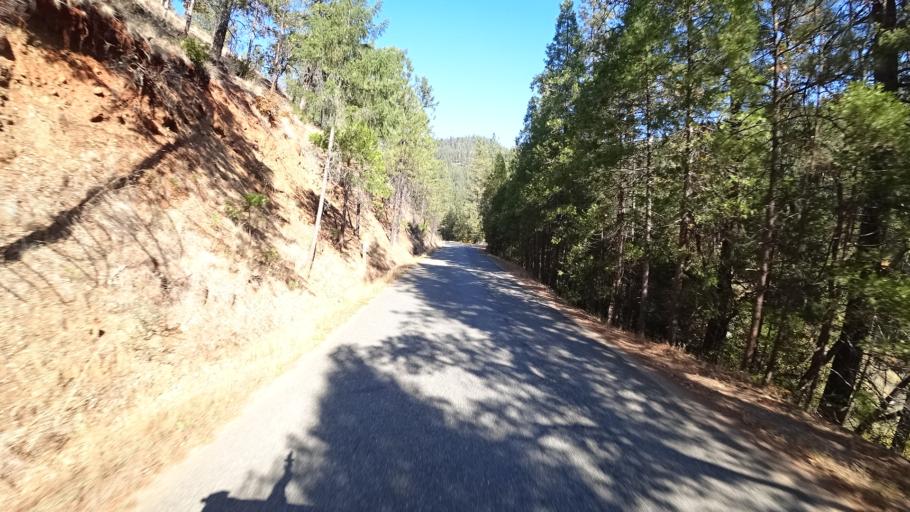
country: US
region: California
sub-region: Siskiyou County
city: Happy Camp
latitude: 41.7590
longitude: -123.0145
